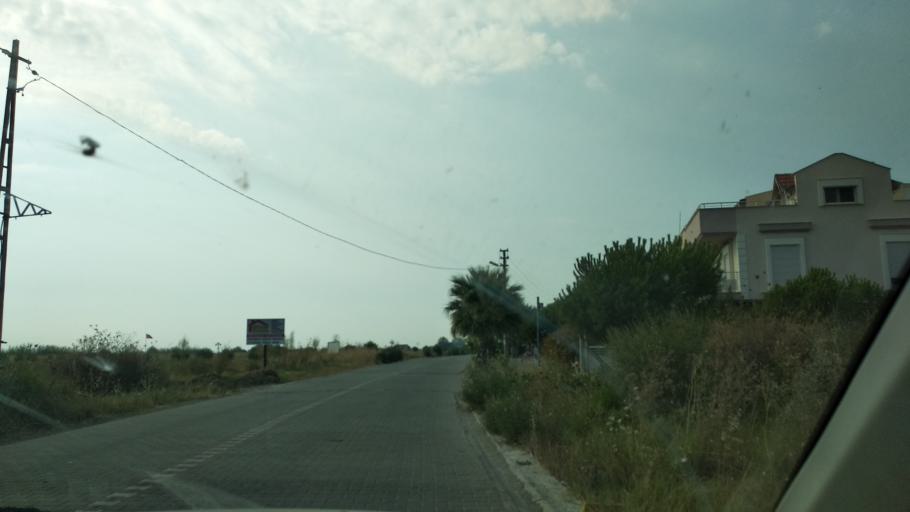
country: TR
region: Izmir
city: Dikili
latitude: 39.1066
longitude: 26.8721
